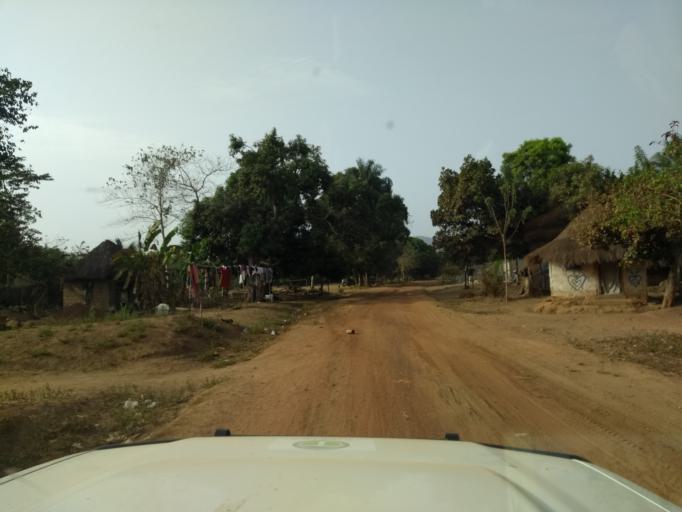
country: GN
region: Kindia
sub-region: Prefecture de Dubreka
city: Dubreka
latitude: 9.8737
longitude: -13.5418
